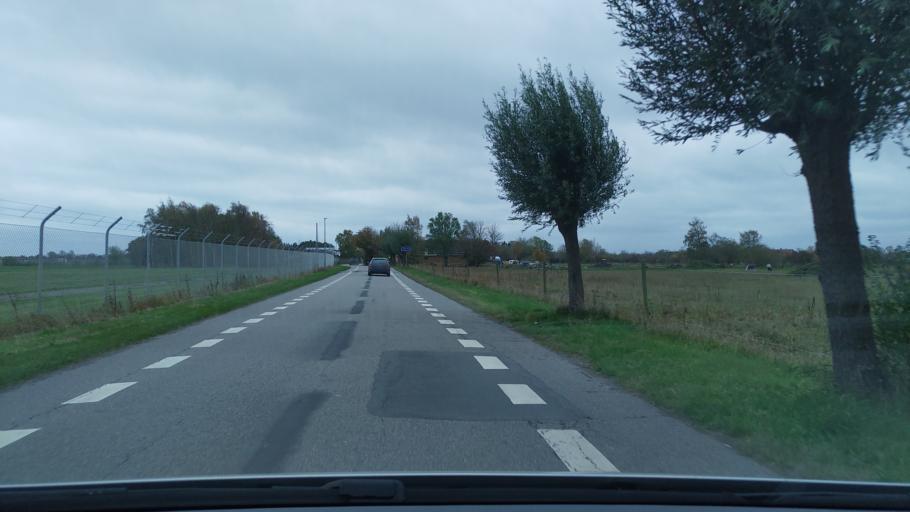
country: DK
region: Capital Region
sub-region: Tarnby Kommune
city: Tarnby
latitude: 55.5957
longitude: 12.5985
